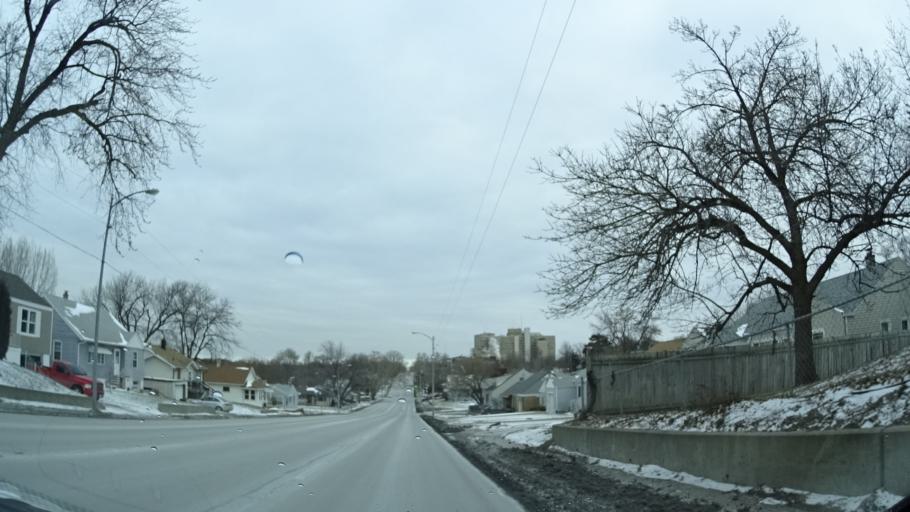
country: US
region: Nebraska
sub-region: Douglas County
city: Omaha
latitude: 41.2359
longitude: -95.9758
